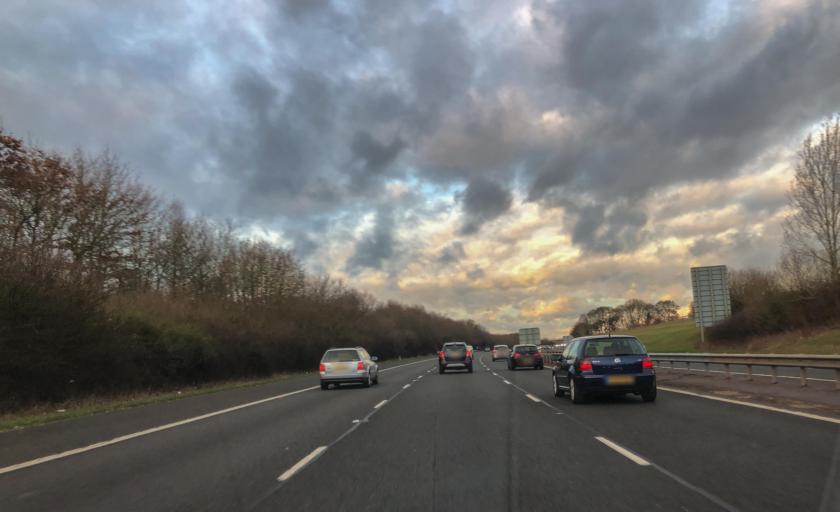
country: GB
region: England
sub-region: Oxfordshire
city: Wheatley
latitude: 51.7562
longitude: -1.1065
